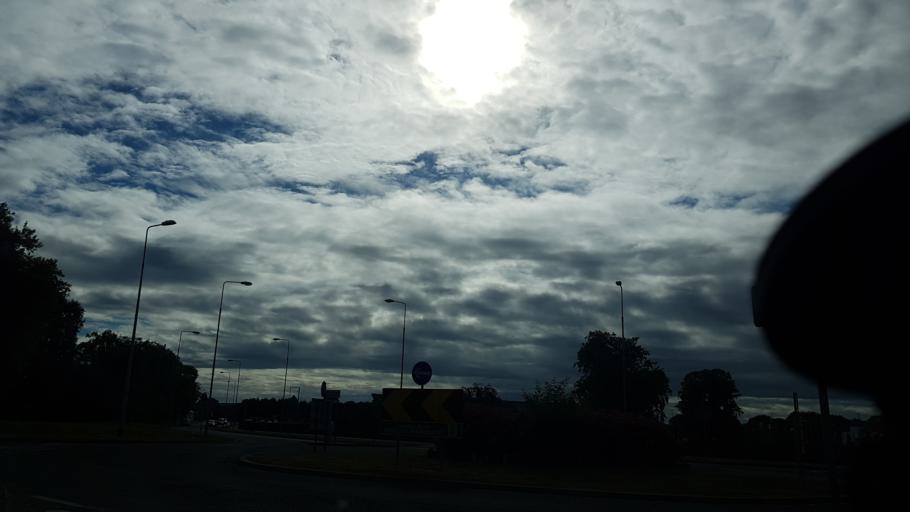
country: IE
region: Munster
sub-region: North Tipperary
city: Nenagh
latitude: 52.8604
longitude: -8.2198
